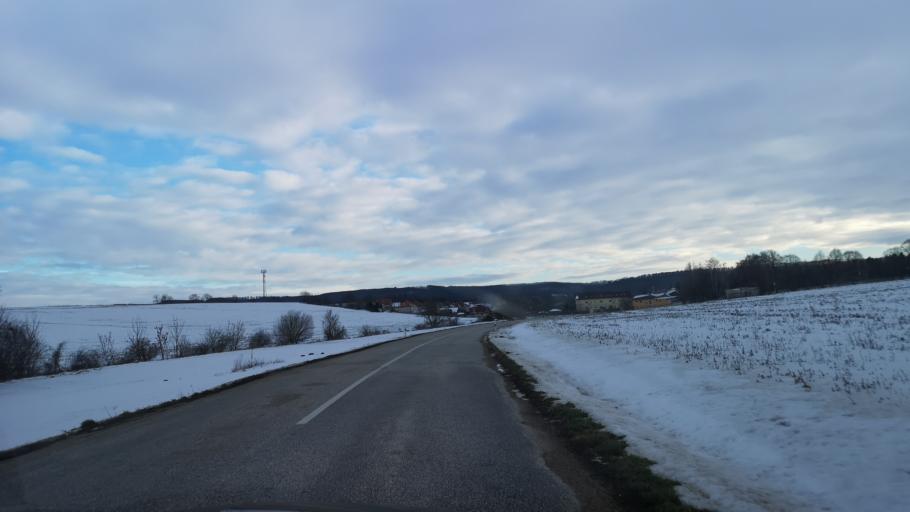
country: SK
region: Nitriansky
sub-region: Okres Nitra
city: Vrable
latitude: 48.1169
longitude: 18.3354
